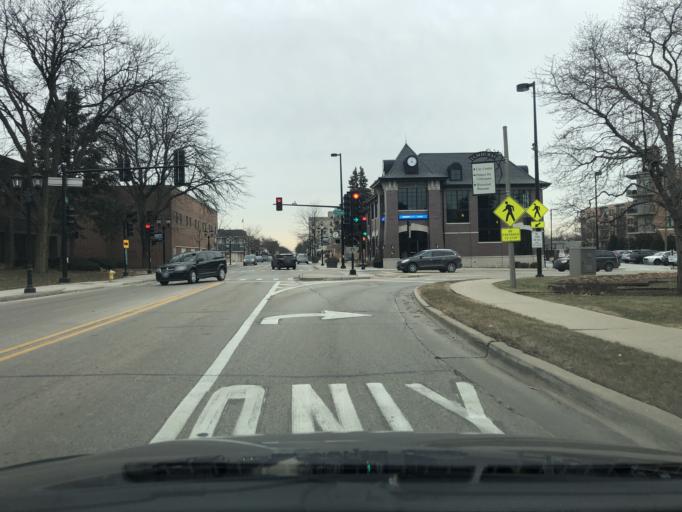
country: US
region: Illinois
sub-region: DuPage County
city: Elmhurst
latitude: 41.8966
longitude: -87.9401
